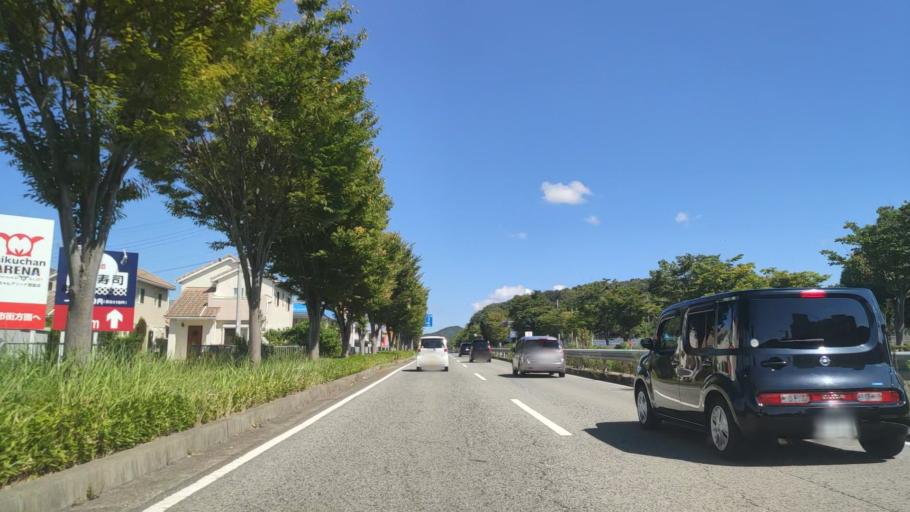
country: JP
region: Hyogo
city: Yashiro
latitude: 34.9416
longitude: 134.9666
